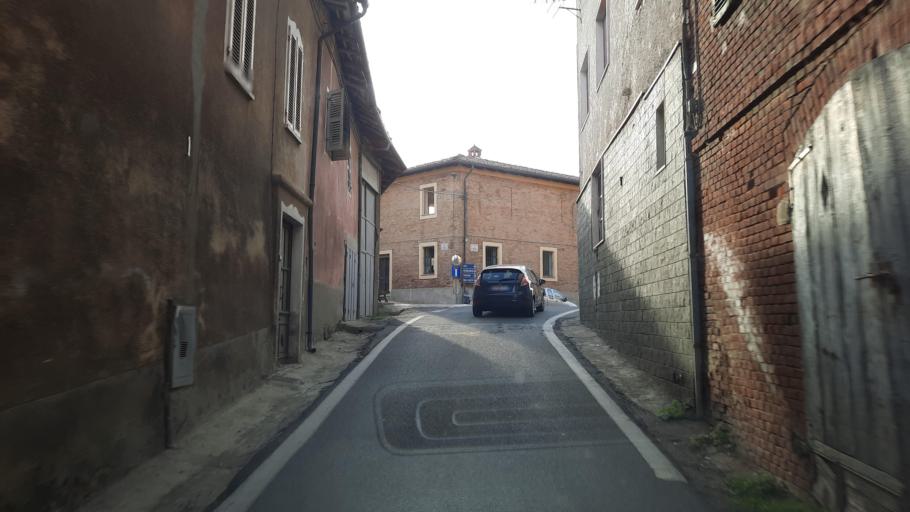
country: IT
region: Piedmont
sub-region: Provincia di Asti
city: Tonco
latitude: 45.0228
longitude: 8.1889
